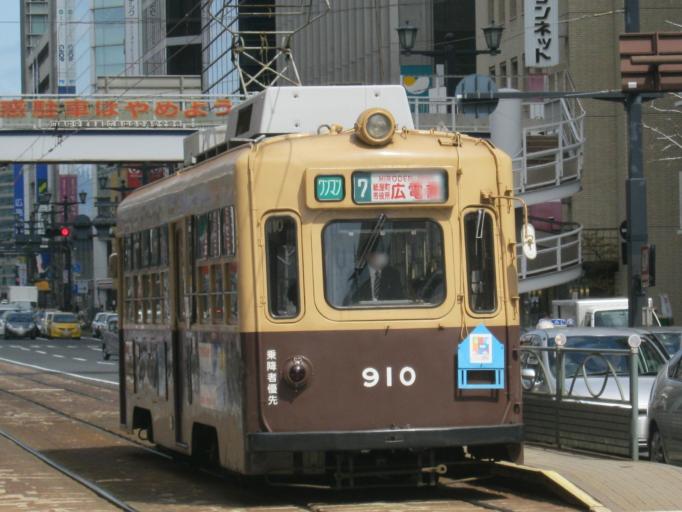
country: JP
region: Hiroshima
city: Hiroshima-shi
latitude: 34.3932
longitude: 132.4671
